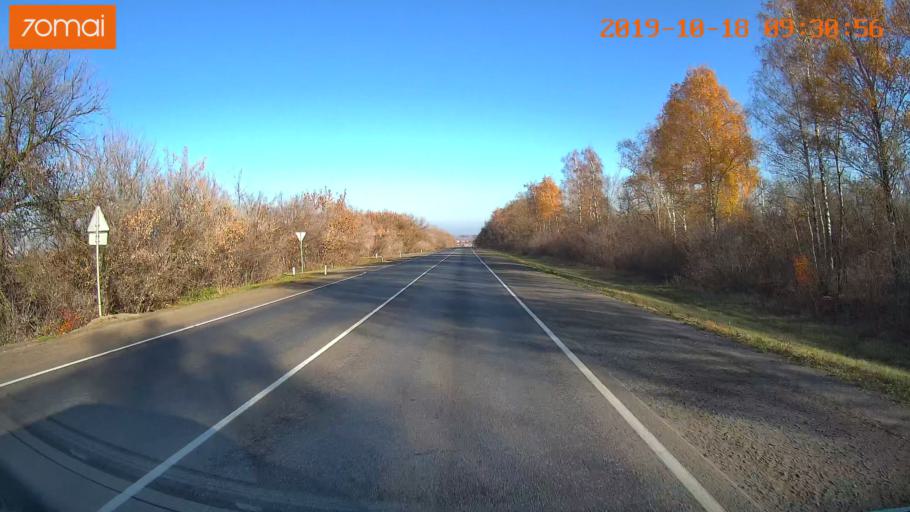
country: RU
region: Tula
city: Yefremov
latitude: 53.1443
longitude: 38.1589
